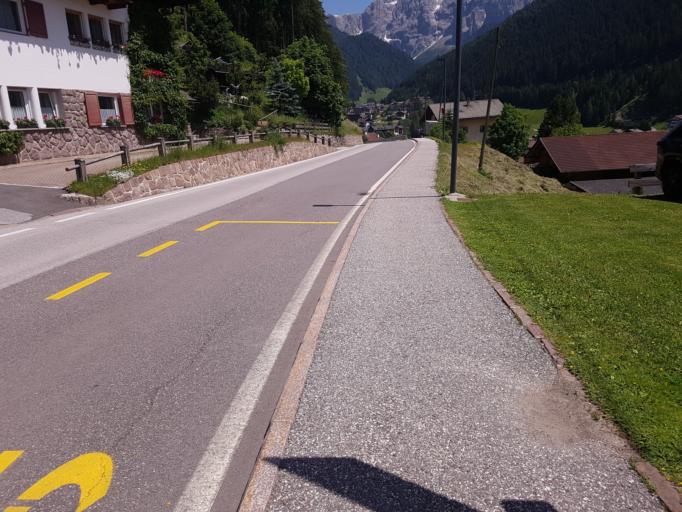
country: IT
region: Trentino-Alto Adige
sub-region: Bolzano
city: Santa Cristina Valgardena
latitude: 46.5606
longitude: 11.7389
